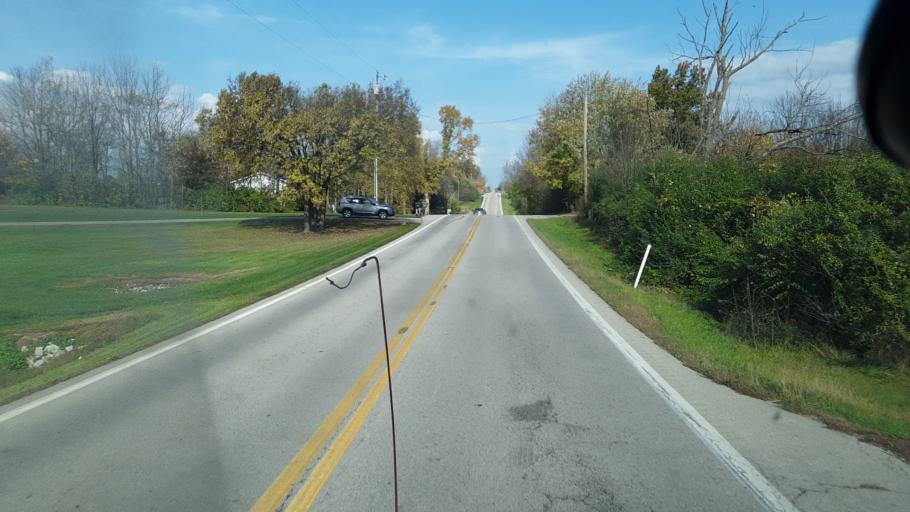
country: US
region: Ohio
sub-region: Clinton County
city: Sabina
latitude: 39.5116
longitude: -83.6895
